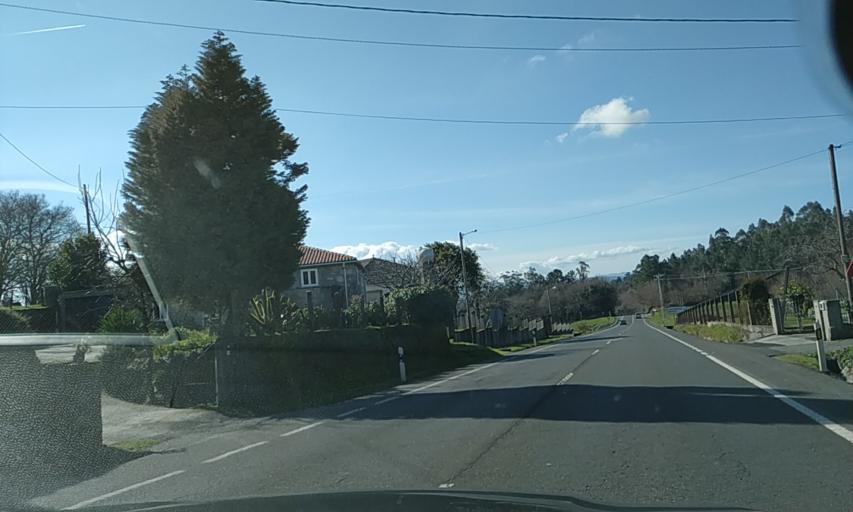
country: ES
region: Galicia
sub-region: Provincia da Coruna
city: Ribeira
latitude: 42.7068
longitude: -8.4131
